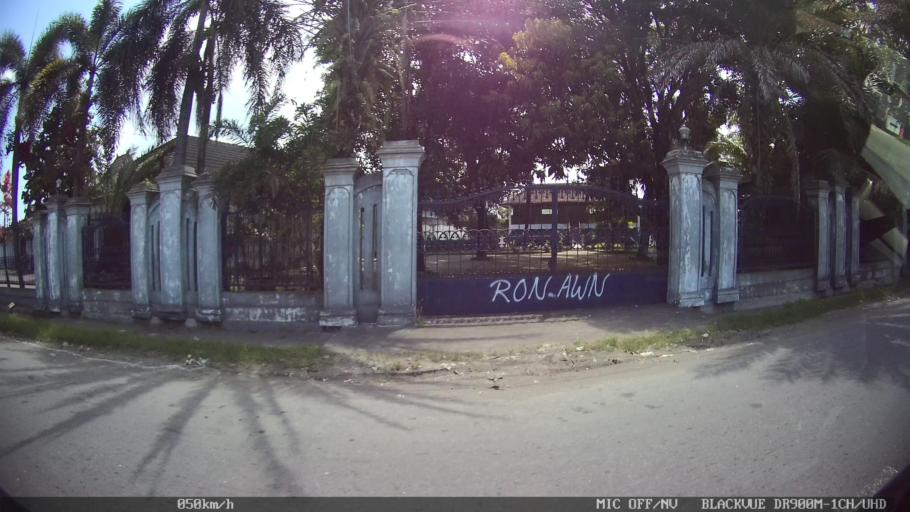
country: ID
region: Daerah Istimewa Yogyakarta
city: Pandak
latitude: -7.9063
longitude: 110.3095
